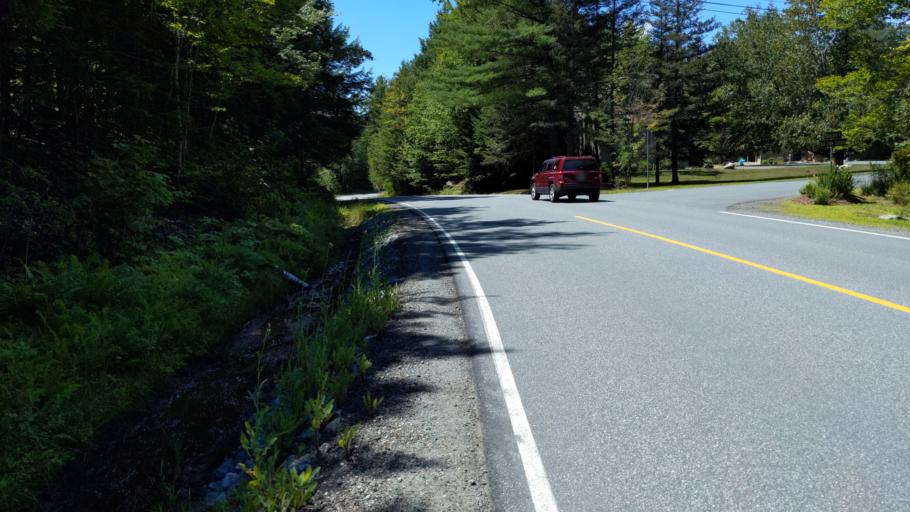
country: US
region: New Hampshire
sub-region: Sullivan County
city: Grantham
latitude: 43.5149
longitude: -72.1112
